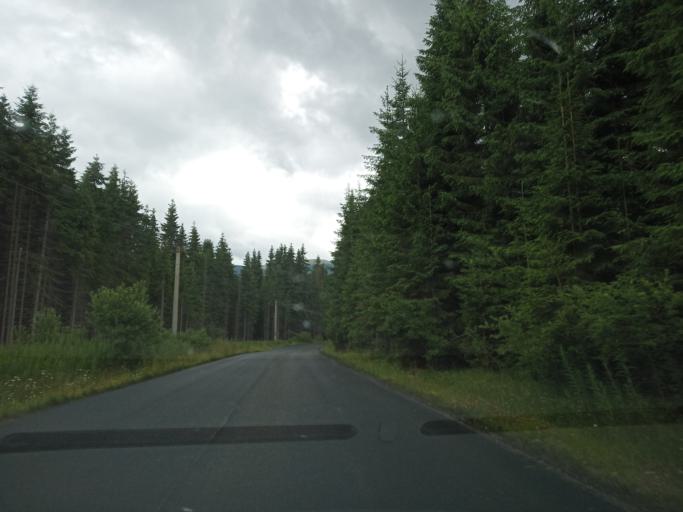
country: RO
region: Gorj
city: Novaci-Straini
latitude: 45.4224
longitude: 23.6955
